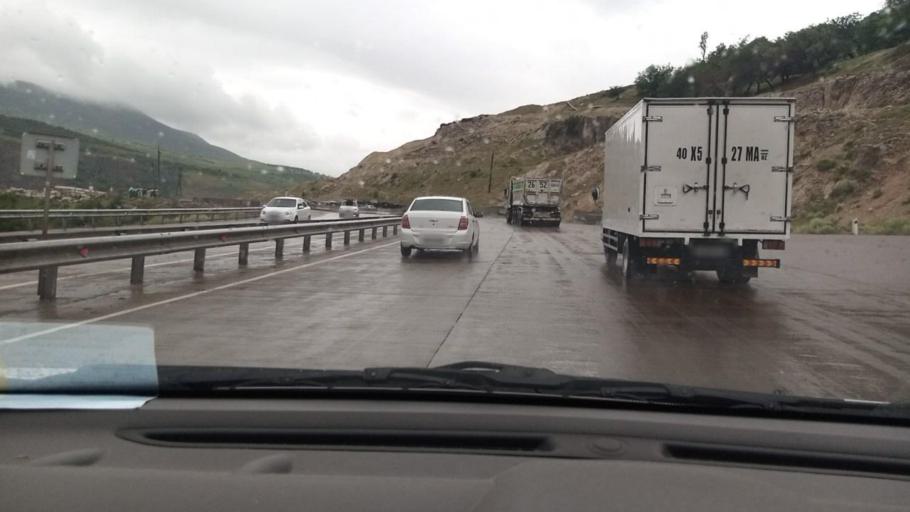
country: UZ
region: Toshkent
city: Angren
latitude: 41.0747
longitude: 70.2518
